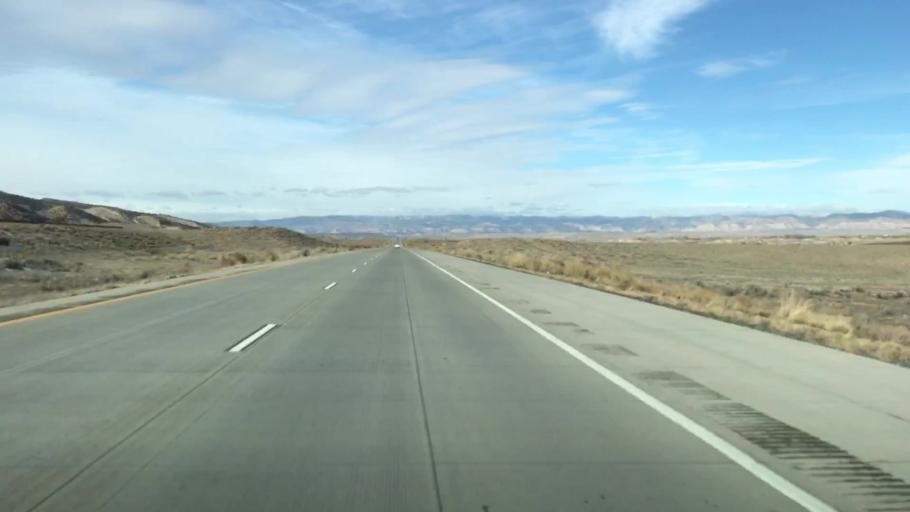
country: US
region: Colorado
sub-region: Mesa County
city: Loma
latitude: 39.1938
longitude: -108.8420
